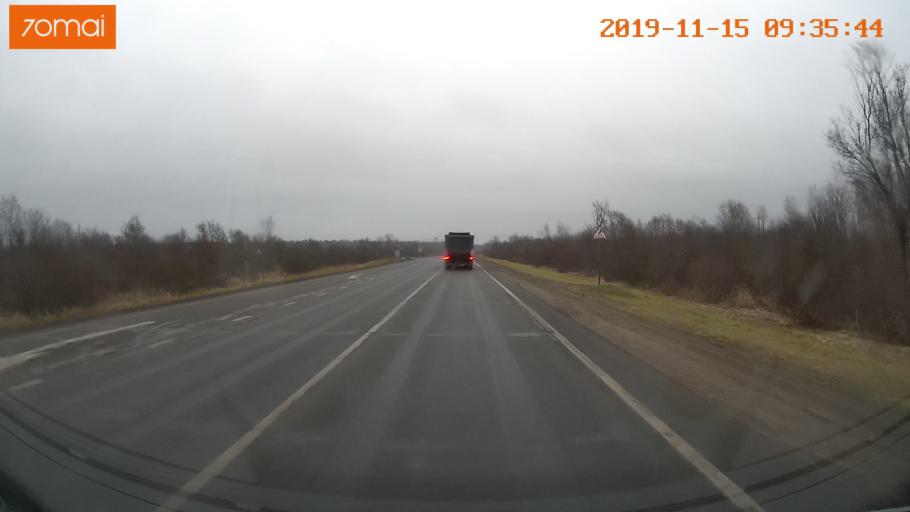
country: RU
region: Vologda
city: Sheksna
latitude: 59.2525
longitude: 38.4057
